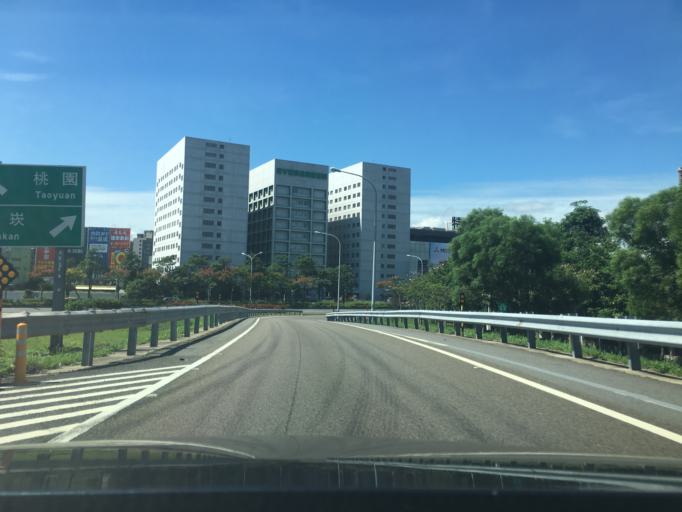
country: TW
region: Taiwan
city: Taoyuan City
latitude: 25.0396
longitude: 121.2976
